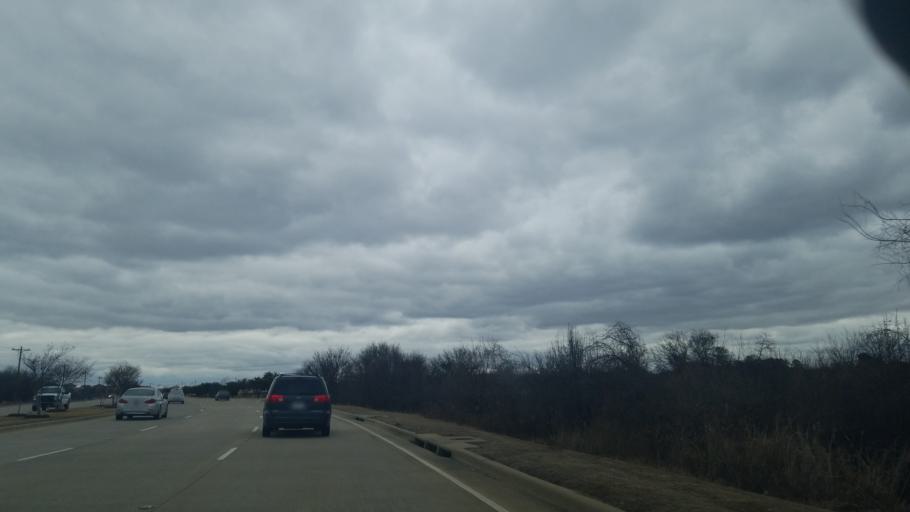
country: US
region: Texas
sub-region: Denton County
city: Double Oak
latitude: 33.0610
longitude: -97.0758
